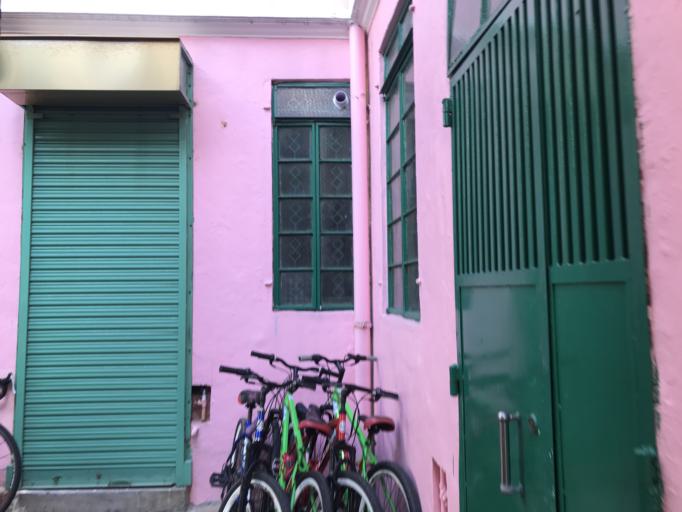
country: MO
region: Macau
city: Macau
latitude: 22.1535
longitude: 113.5567
